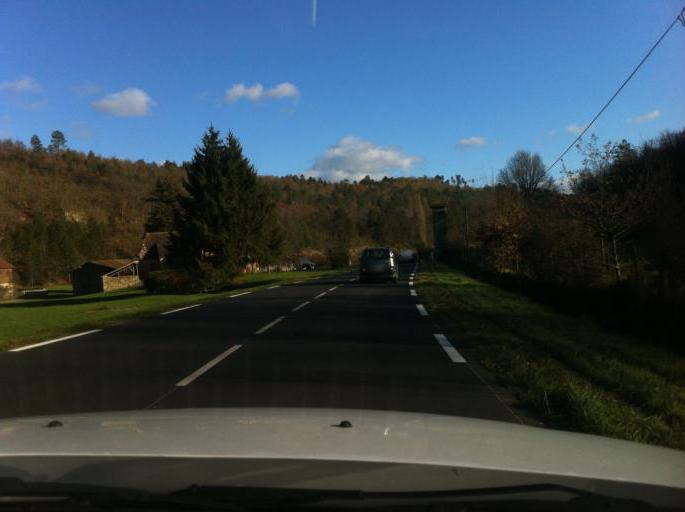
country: FR
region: Aquitaine
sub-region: Departement de la Dordogne
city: Rouffignac-Saint-Cernin-de-Reilhac
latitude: 45.0246
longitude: 0.9108
